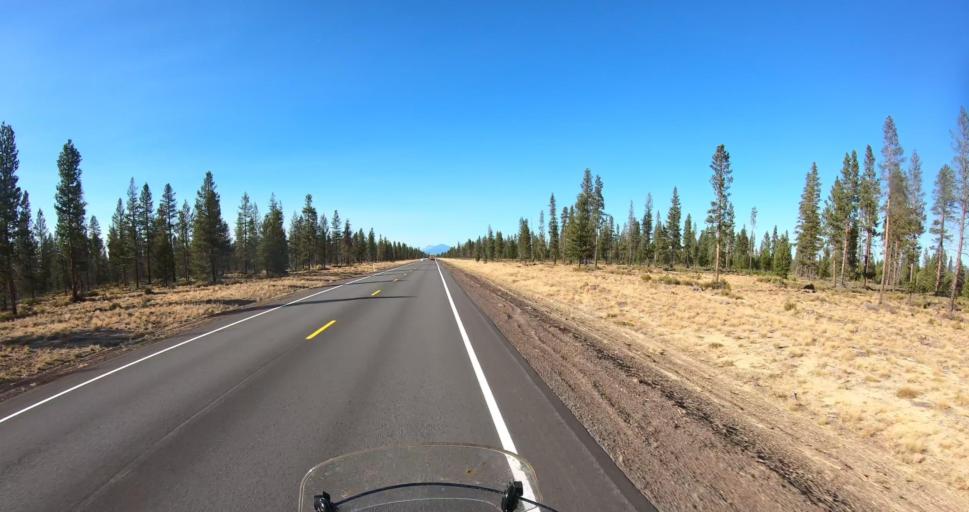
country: US
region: Oregon
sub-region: Deschutes County
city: La Pine
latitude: 43.5757
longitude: -121.4847
